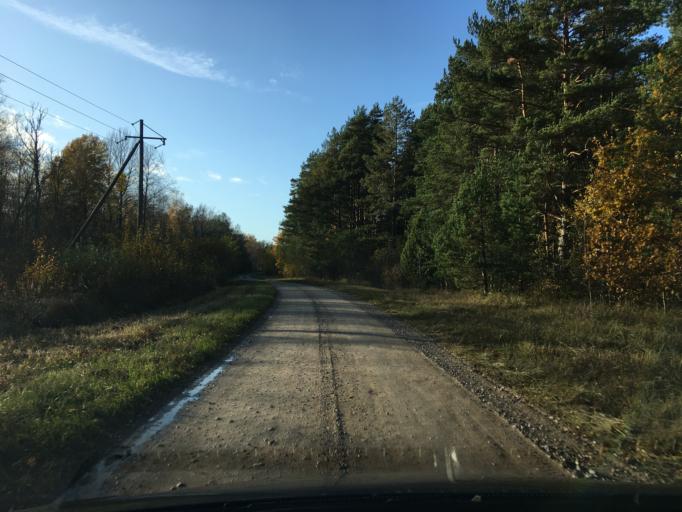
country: EE
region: Laeaene
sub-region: Lihula vald
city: Lihula
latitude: 58.5680
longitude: 23.7601
